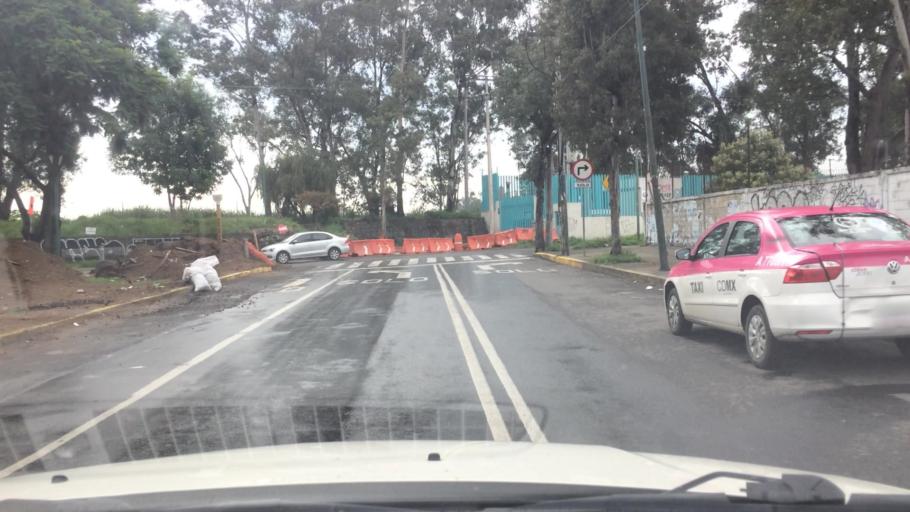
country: MX
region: Mexico City
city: Xochimilco
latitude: 19.3067
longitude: -99.1007
